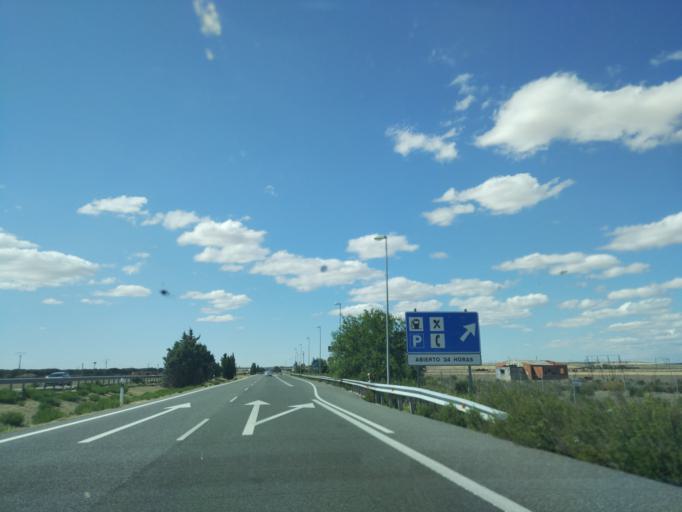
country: ES
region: Castille and Leon
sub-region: Provincia de Valladolid
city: Medina del Campo
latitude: 41.2704
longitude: -4.8849
